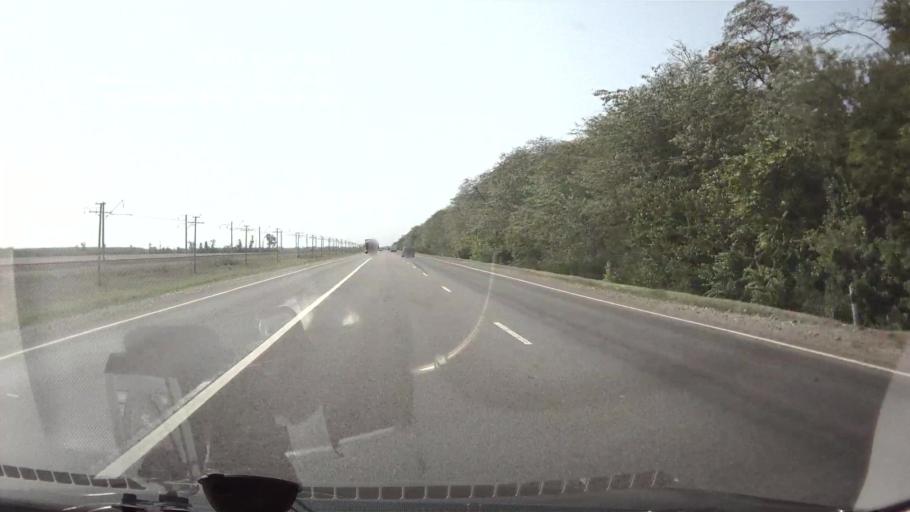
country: RU
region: Krasnodarskiy
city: Dvubratskiy
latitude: 45.2870
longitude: 39.8572
